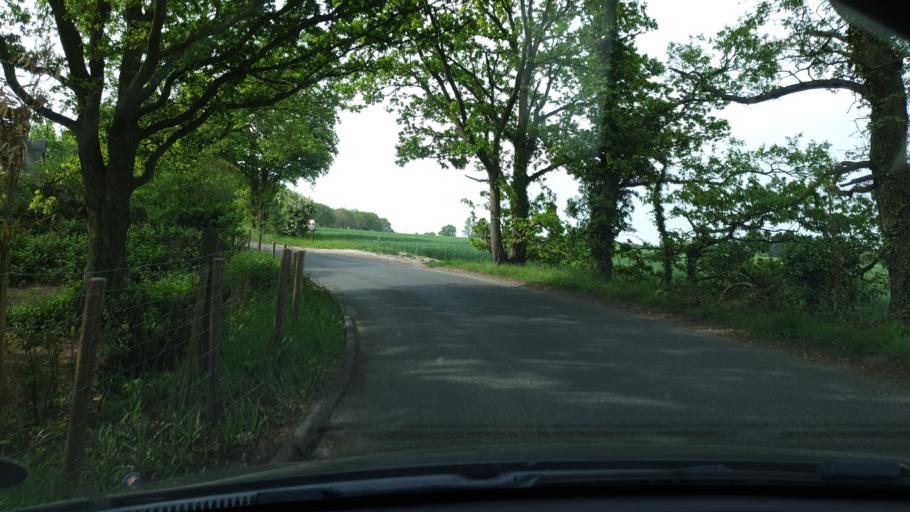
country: GB
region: England
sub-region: Essex
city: Great Bentley
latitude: 51.8735
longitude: 1.0800
